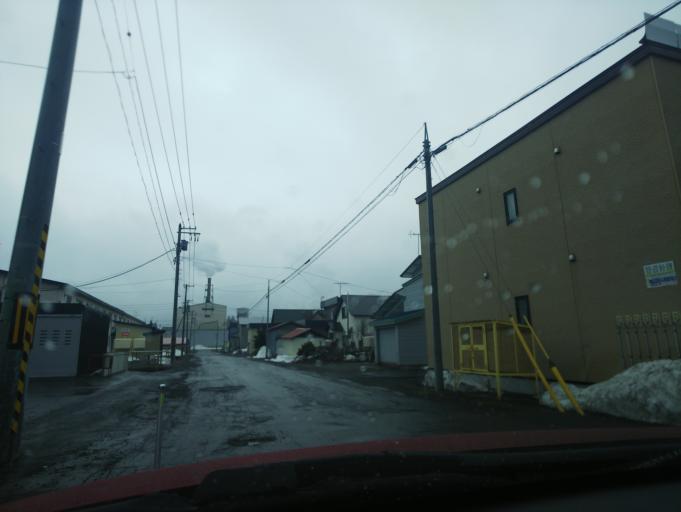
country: JP
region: Hokkaido
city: Nayoro
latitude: 44.3430
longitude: 142.4605
